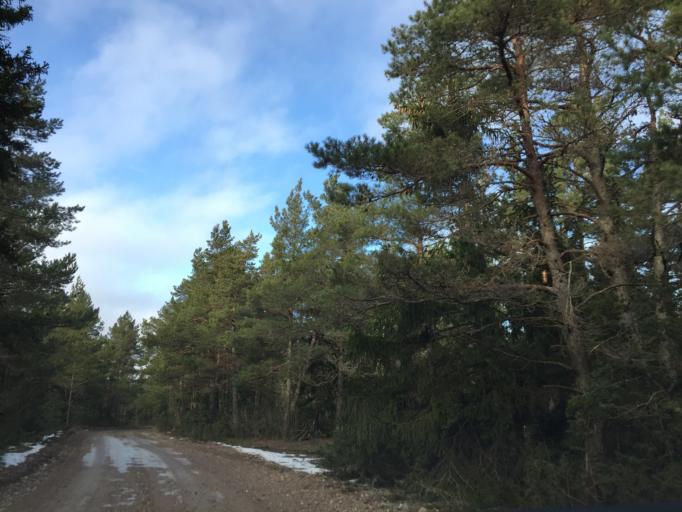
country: EE
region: Saare
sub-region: Kuressaare linn
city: Kuressaare
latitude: 58.4818
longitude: 21.9472
